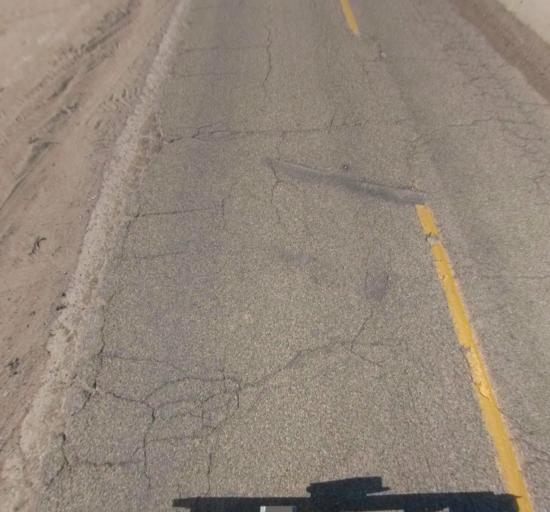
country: US
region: California
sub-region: Madera County
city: Parkwood
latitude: 36.8544
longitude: -120.1284
